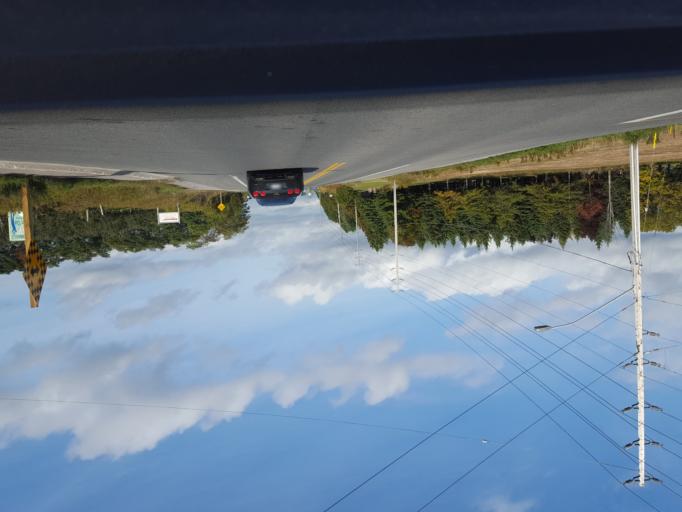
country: CA
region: Ontario
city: Oshawa
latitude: 43.9701
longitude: -78.7180
